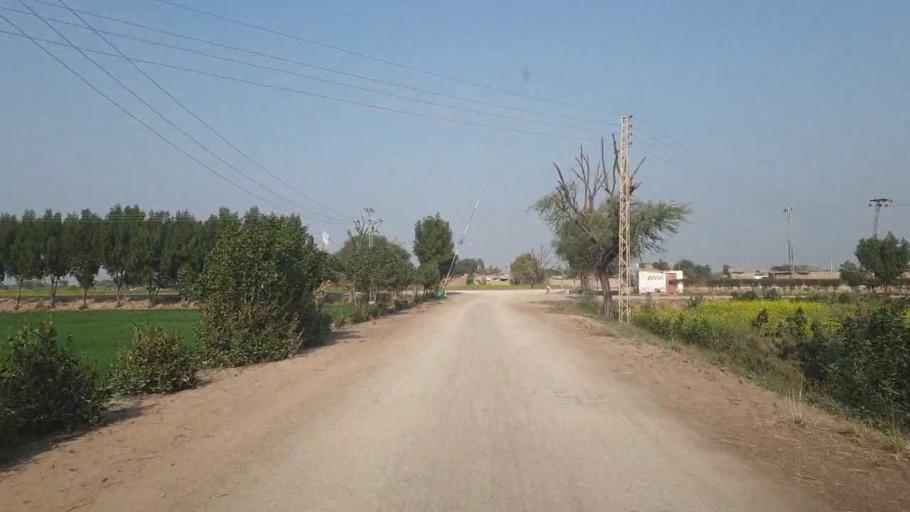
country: PK
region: Sindh
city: Tando Allahyar
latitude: 25.4387
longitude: 68.7075
